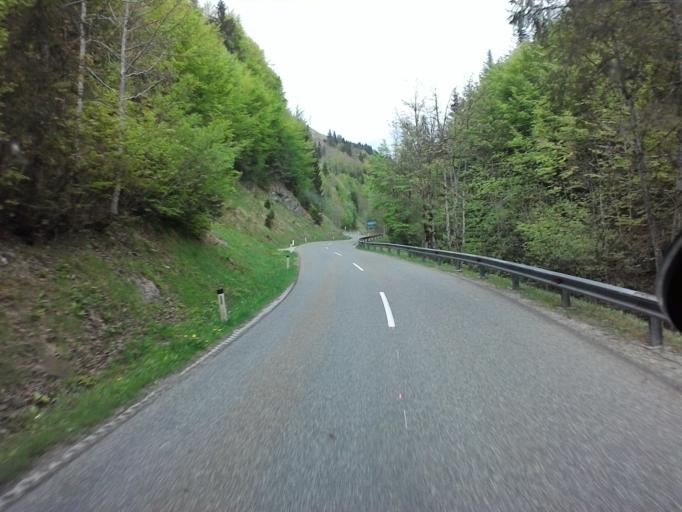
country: AT
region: Styria
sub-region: Politischer Bezirk Liezen
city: Hall
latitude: 47.7138
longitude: 14.4213
